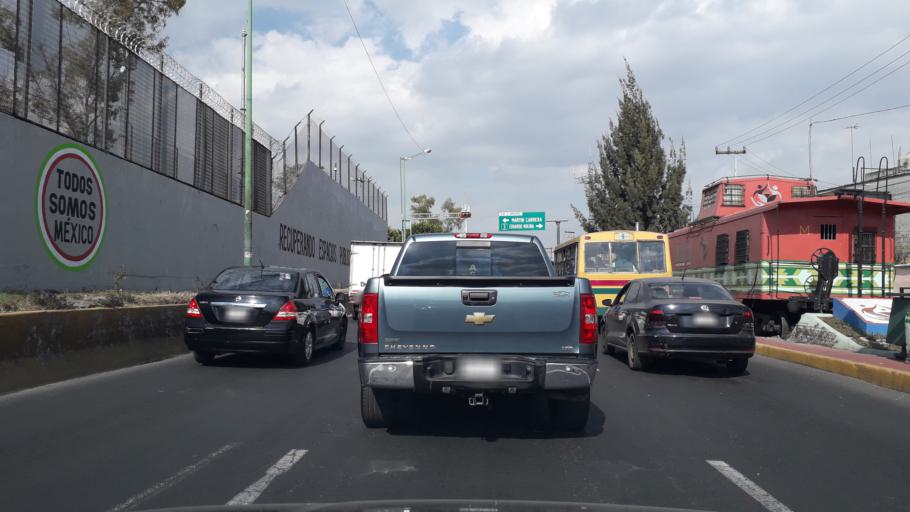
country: MX
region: Mexico City
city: Gustavo A. Madero
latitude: 19.4890
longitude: -99.1012
